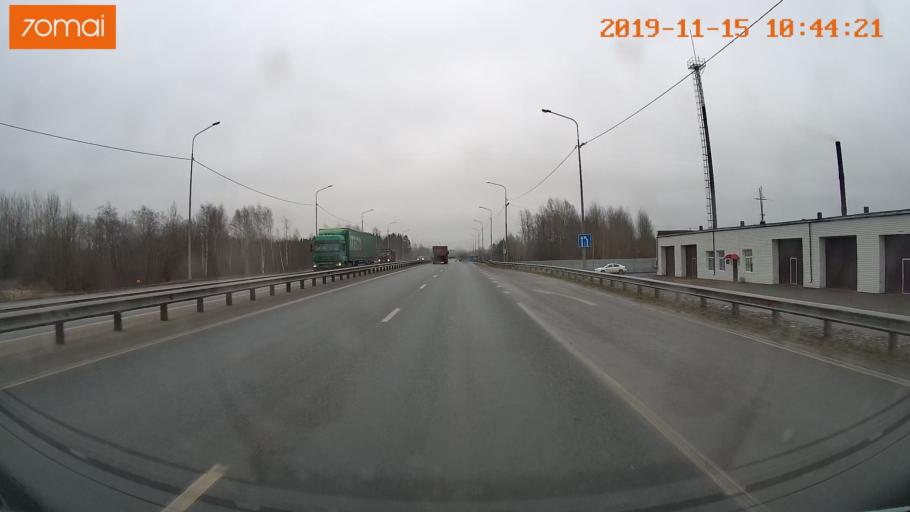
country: RU
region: Vologda
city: Sheksna
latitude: 59.2115
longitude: 38.5554
